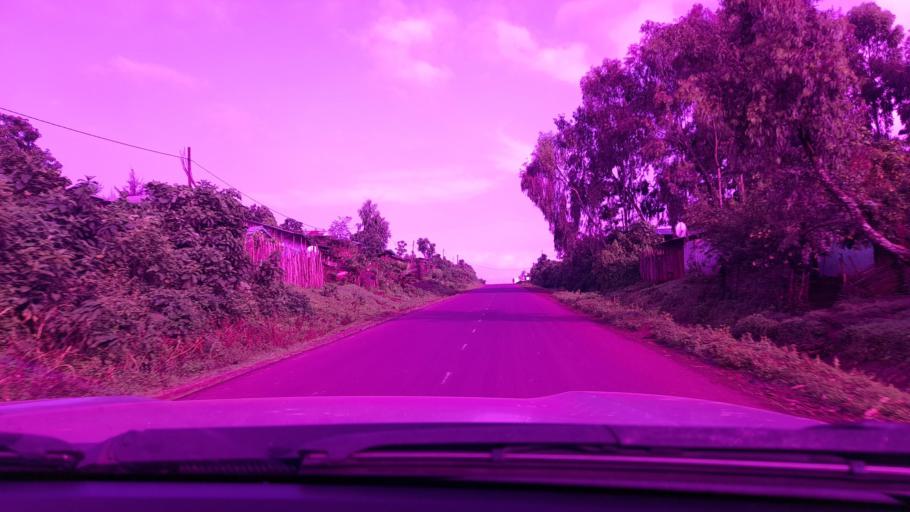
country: ET
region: Oromiya
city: Bedele
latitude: 8.1691
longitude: 36.4657
